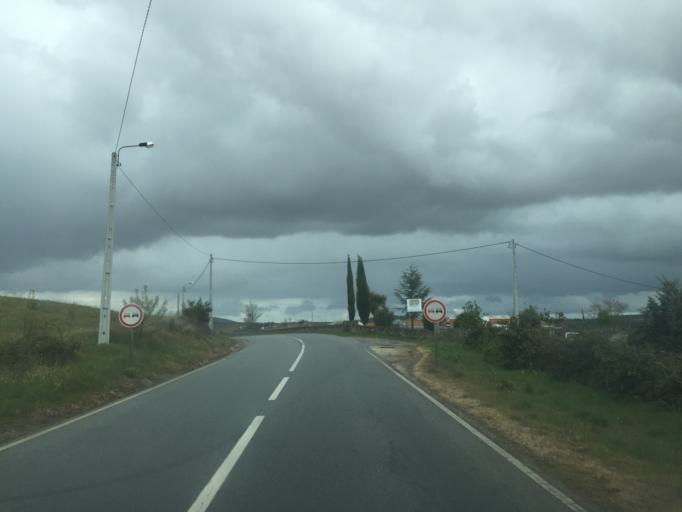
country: PT
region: Braganca
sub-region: Mogadouro
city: Mogadouro
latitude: 41.3409
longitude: -6.6964
